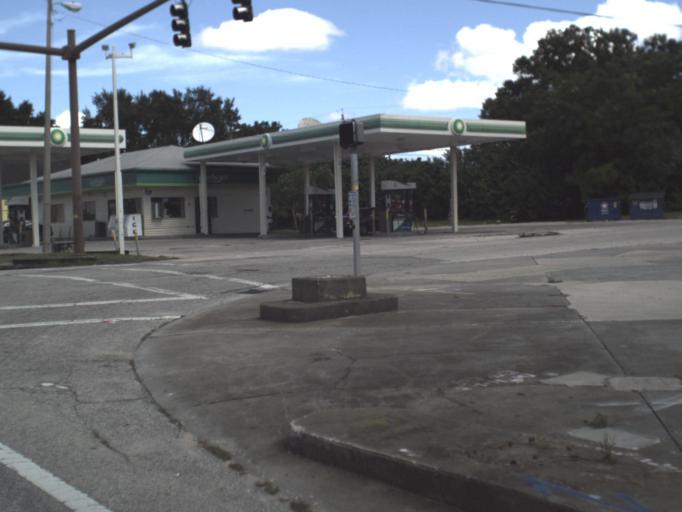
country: US
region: Florida
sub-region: Polk County
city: Lake Wales
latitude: 27.9100
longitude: -81.5876
